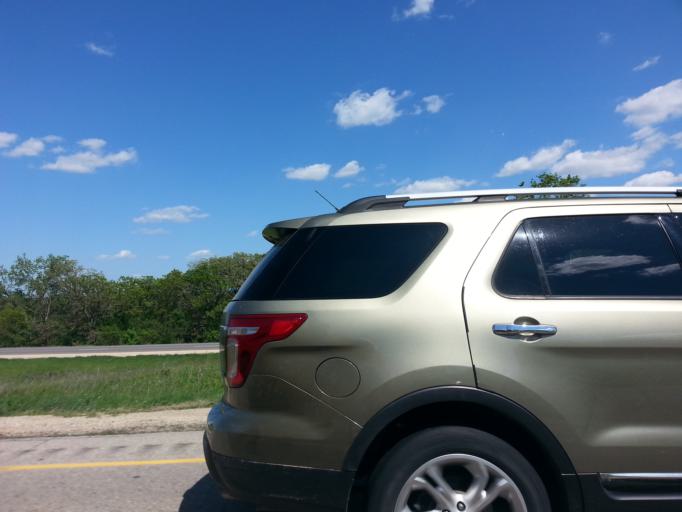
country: US
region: Wisconsin
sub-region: Rock County
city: Milton
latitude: 42.7518
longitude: -89.0053
